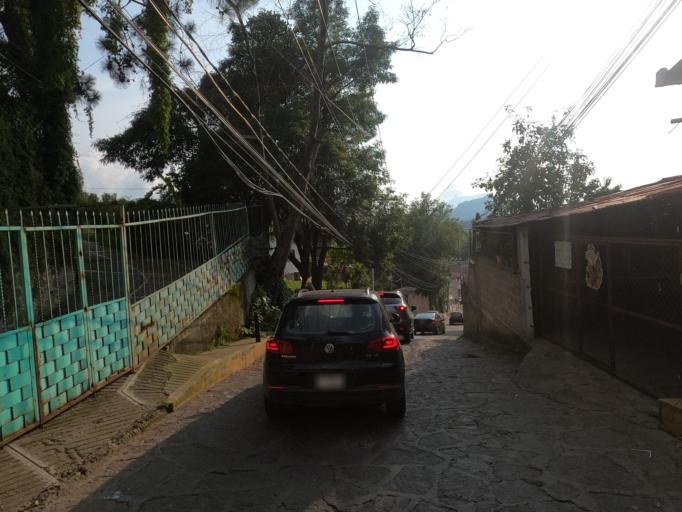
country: MX
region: Mexico
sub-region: Valle de Bravo
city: Colonia Rincon Villa del Valle
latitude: 19.2050
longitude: -100.1197
